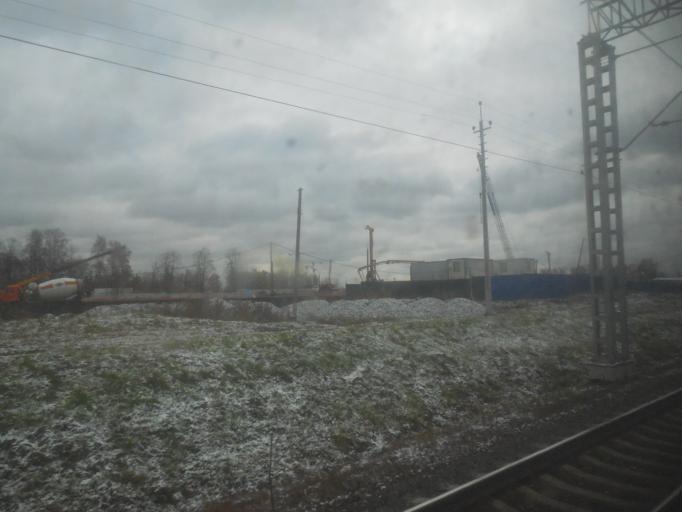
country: RU
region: Moskovskaya
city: Novoivanovskoye
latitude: 55.7007
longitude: 37.3434
